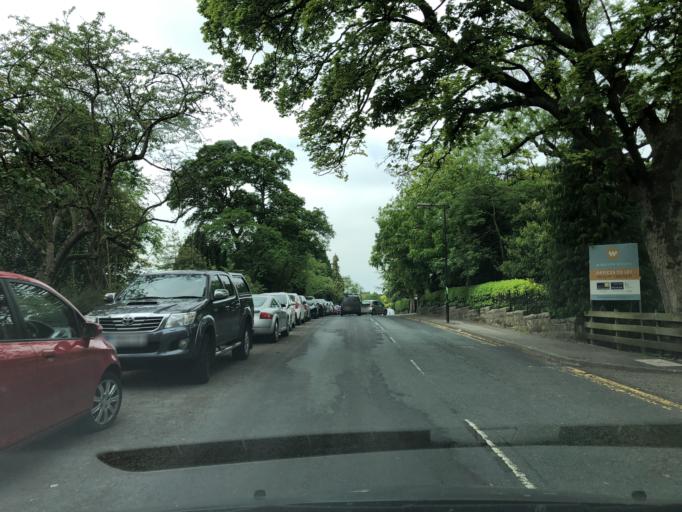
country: GB
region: England
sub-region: North Yorkshire
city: Harrogate
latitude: 53.9932
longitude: -1.5491
